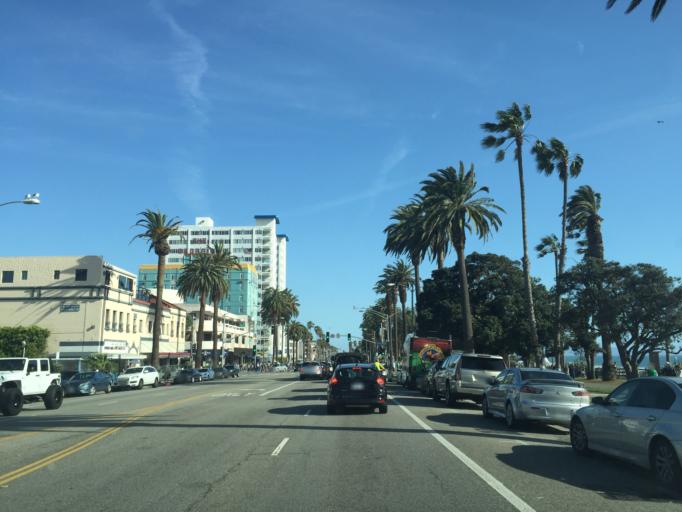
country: US
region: California
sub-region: Los Angeles County
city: Santa Monica
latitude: 34.0147
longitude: -118.4989
